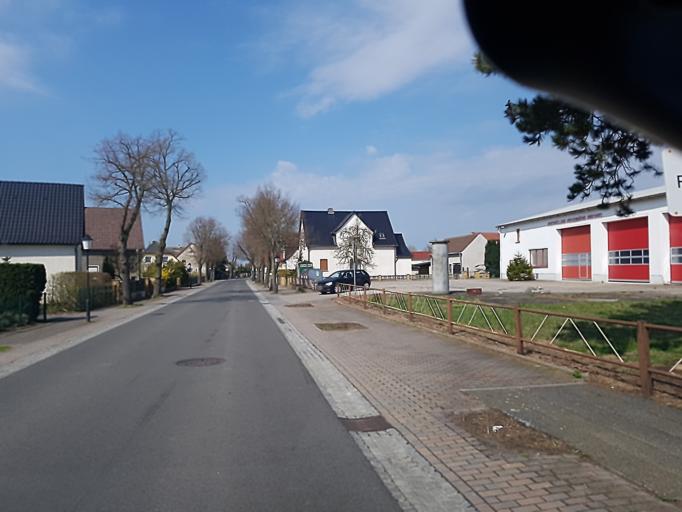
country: DE
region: Saxony
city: Kossa
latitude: 51.5780
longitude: 12.7099
